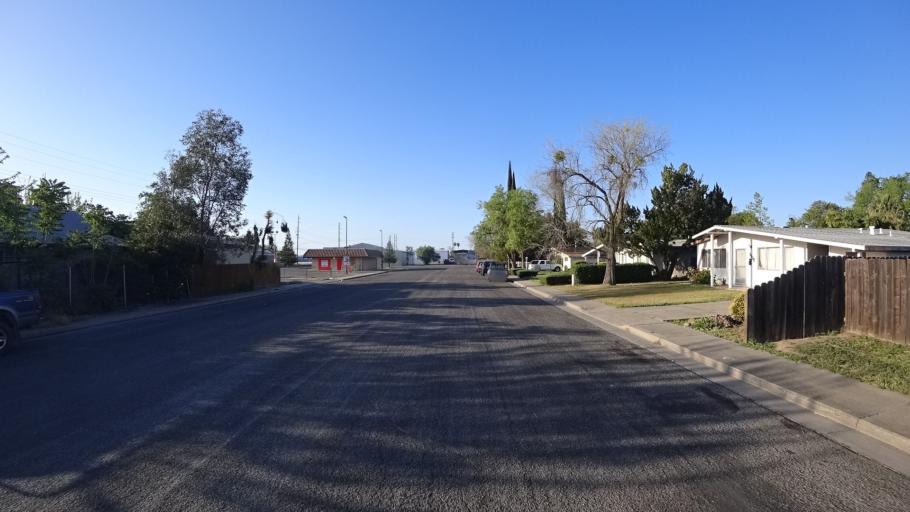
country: US
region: California
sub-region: Glenn County
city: Orland
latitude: 39.7438
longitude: -122.1982
